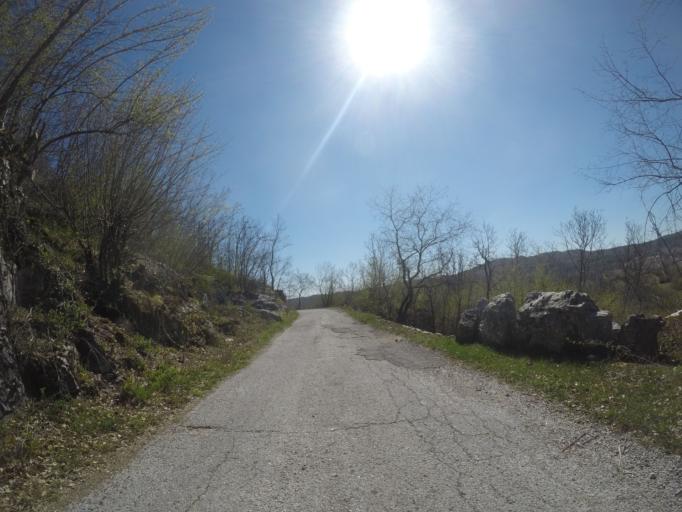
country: ME
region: Cetinje
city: Cetinje
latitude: 42.5281
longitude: 18.9643
